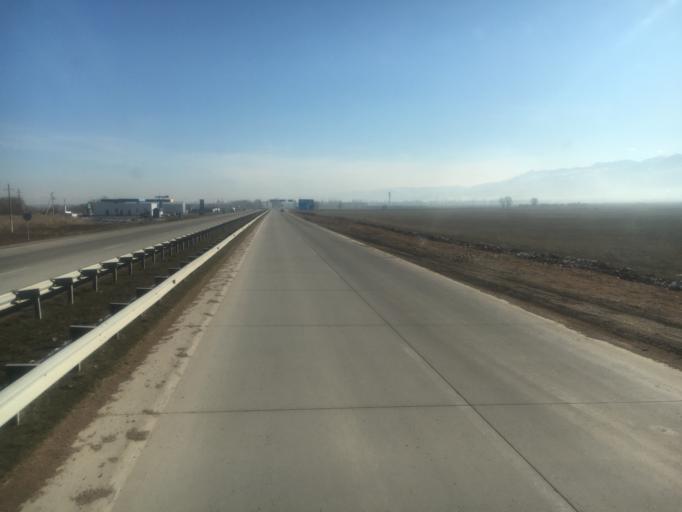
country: KZ
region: Zhambyl
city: Merke
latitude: 42.8753
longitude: 73.1223
